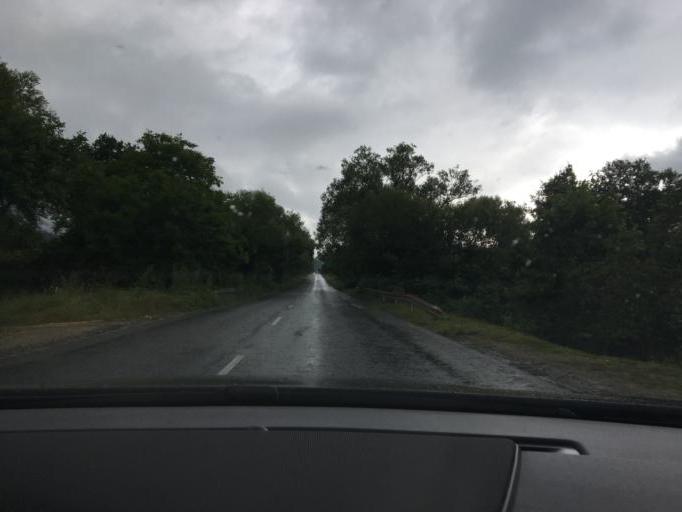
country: BG
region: Kyustendil
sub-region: Obshtina Kyustendil
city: Kyustendil
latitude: 42.2654
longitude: 22.6019
